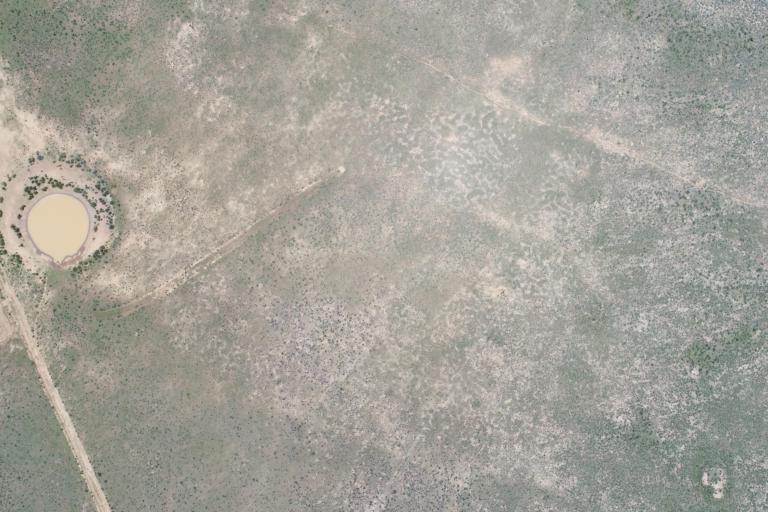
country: BO
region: La Paz
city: Curahuara de Carangas
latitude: -17.3105
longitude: -68.5137
